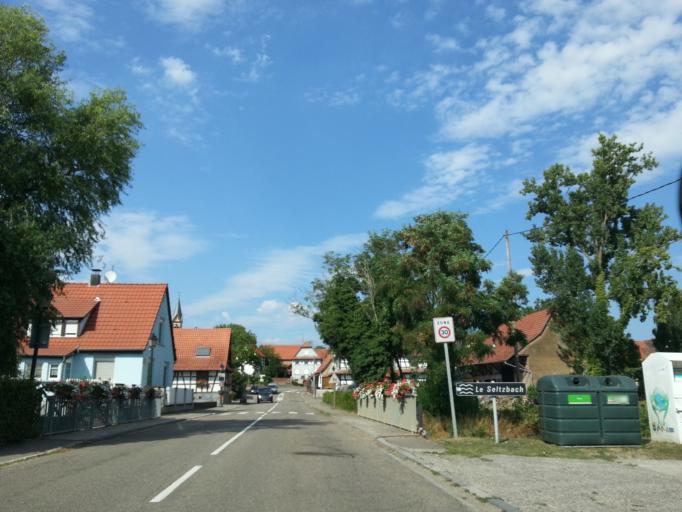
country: FR
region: Alsace
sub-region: Departement du Bas-Rhin
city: Surbourg
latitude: 48.9321
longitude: 7.8548
